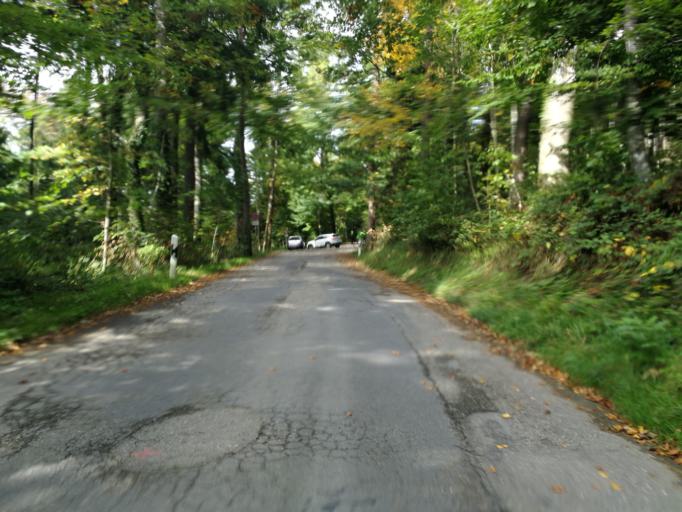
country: CH
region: Zurich
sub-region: Bezirk Uster
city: Egg
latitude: 47.2895
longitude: 8.6745
